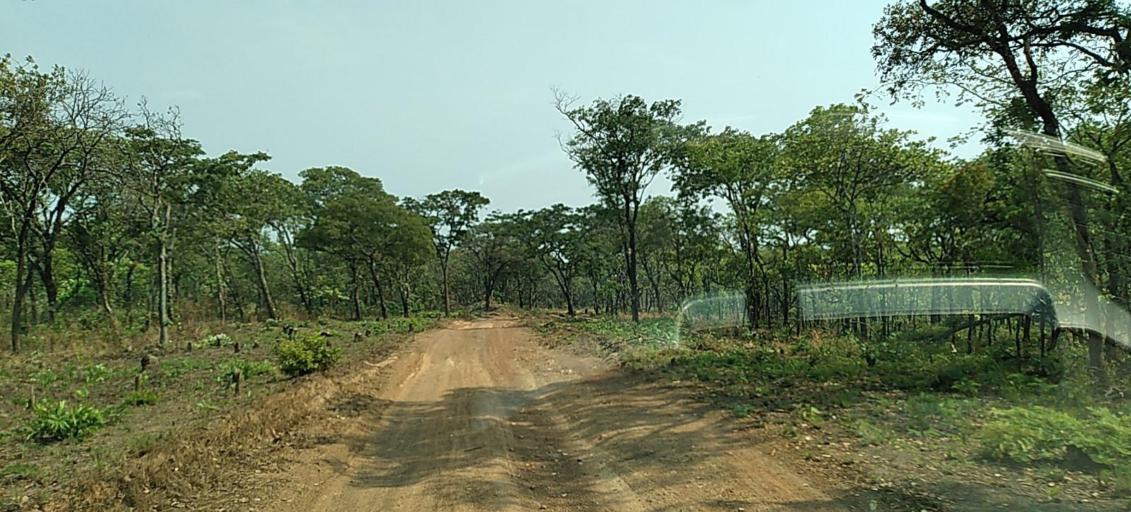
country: ZM
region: North-Western
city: Kansanshi
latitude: -12.0891
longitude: 26.8881
